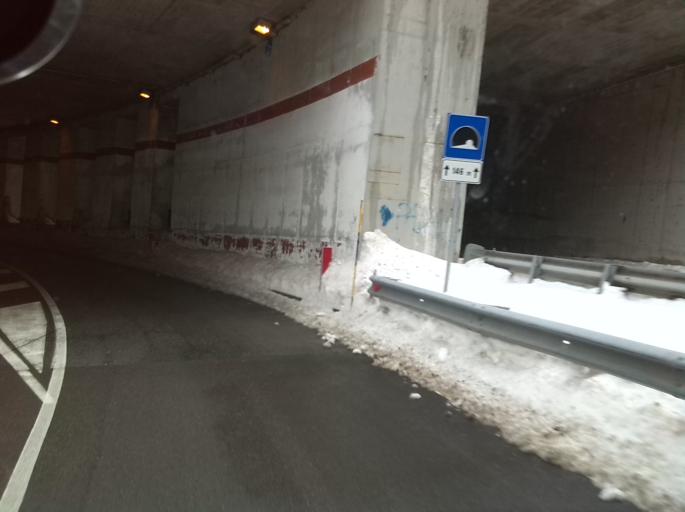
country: IT
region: Friuli Venezia Giulia
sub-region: Provincia di Udine
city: Tarvisio
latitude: 46.5028
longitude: 13.6014
